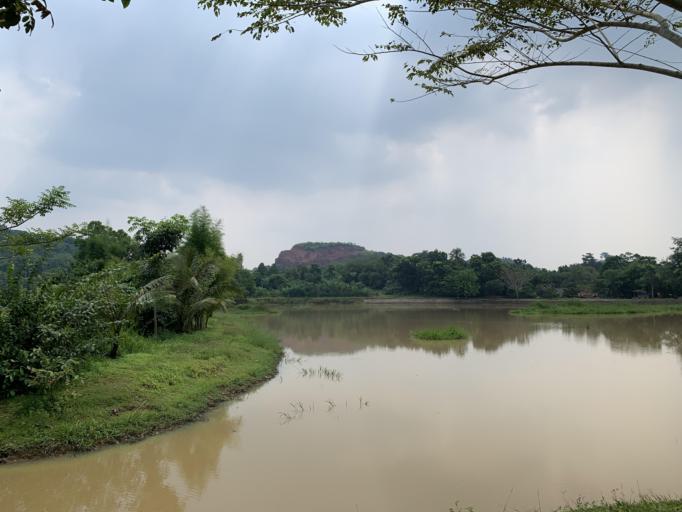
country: ID
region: West Java
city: Serpong
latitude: -6.3802
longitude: 106.5868
